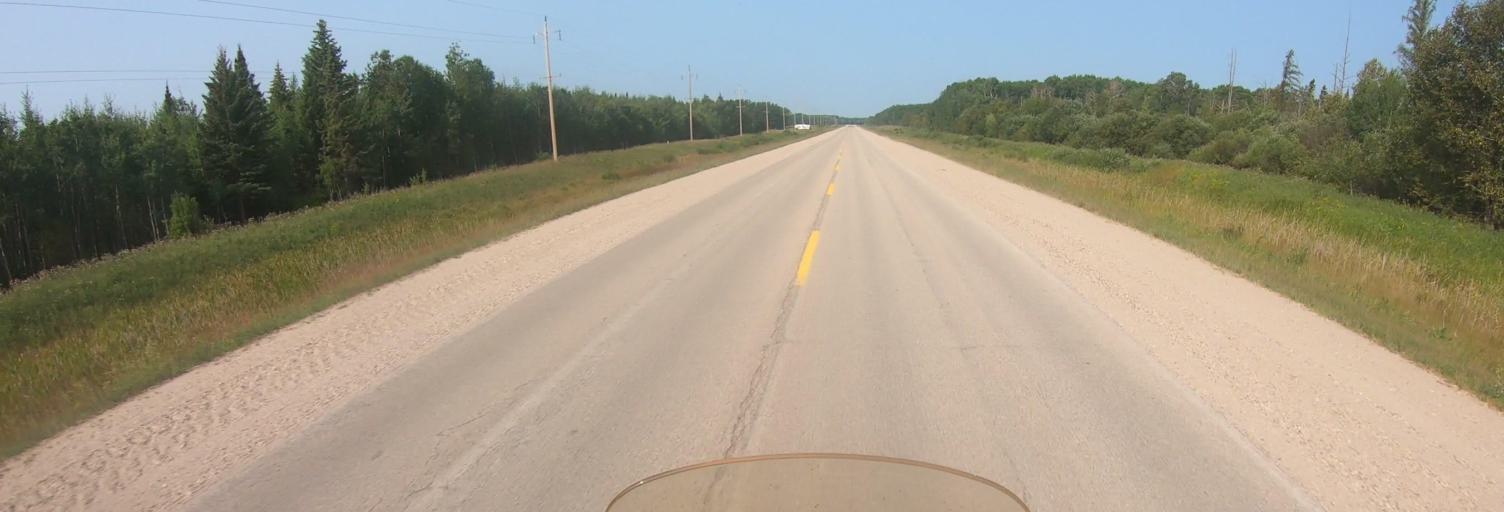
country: US
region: Minnesota
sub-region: Roseau County
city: Roseau
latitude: 49.0235
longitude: -95.7122
